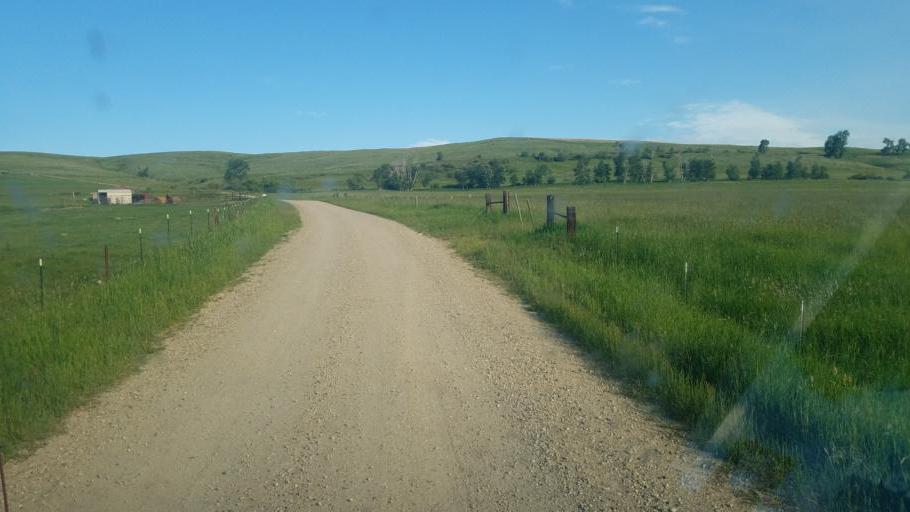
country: US
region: Montana
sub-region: Carbon County
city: Red Lodge
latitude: 45.3627
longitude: -109.1873
